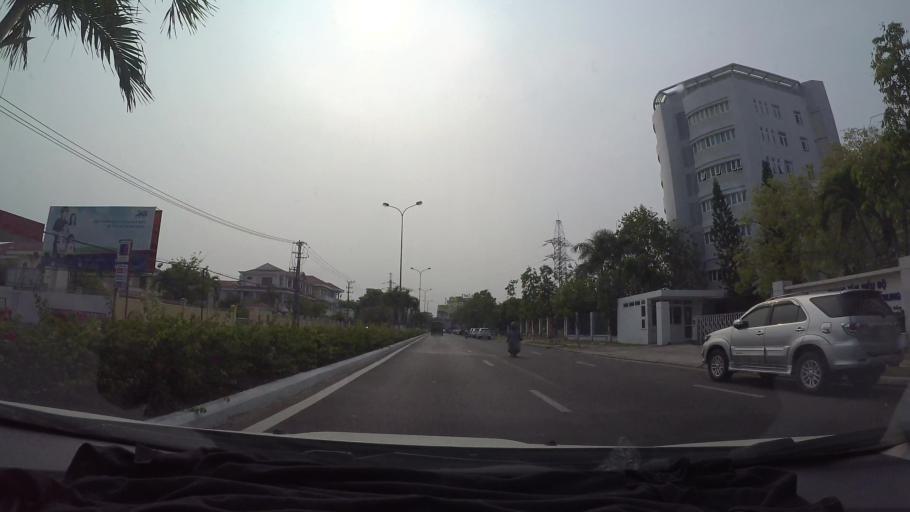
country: VN
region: Da Nang
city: Da Nang
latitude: 16.0485
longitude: 108.2149
